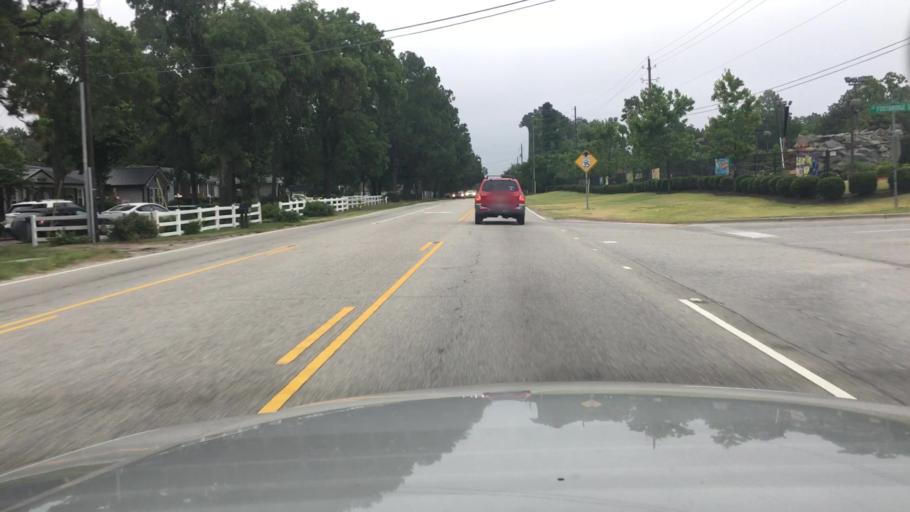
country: US
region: North Carolina
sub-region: Cumberland County
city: Hope Mills
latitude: 34.9819
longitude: -78.9732
